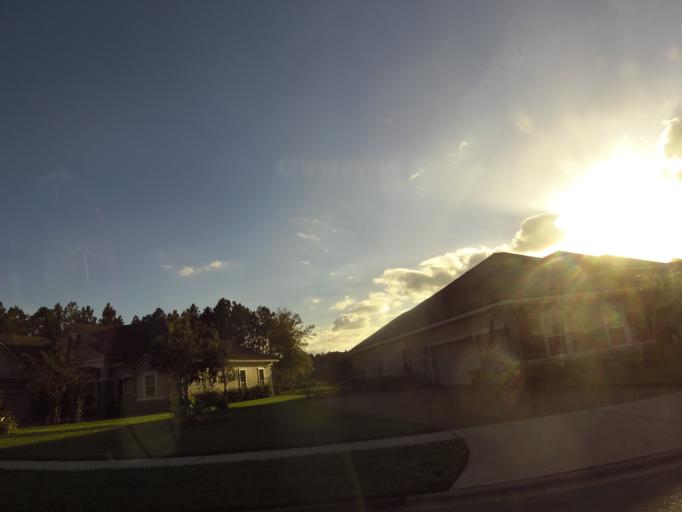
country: US
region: Florida
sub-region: Saint Johns County
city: Fruit Cove
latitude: 30.0637
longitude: -81.6397
